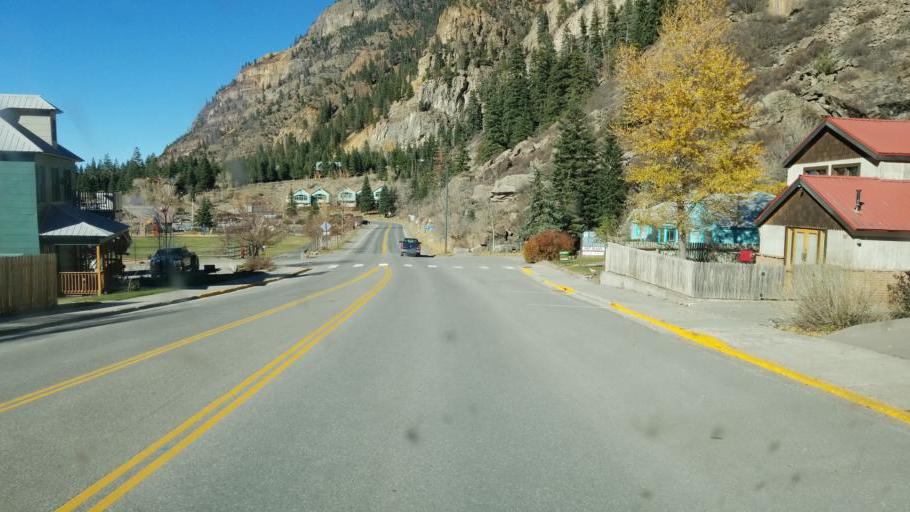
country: US
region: Colorado
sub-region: Ouray County
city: Ouray
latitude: 38.0270
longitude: -107.6714
